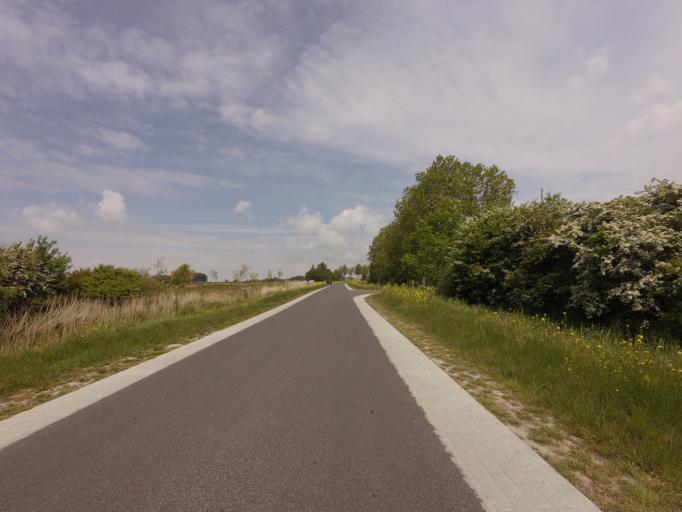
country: NL
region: Friesland
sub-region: Sudwest Fryslan
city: Bolsward
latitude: 53.0982
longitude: 5.4788
